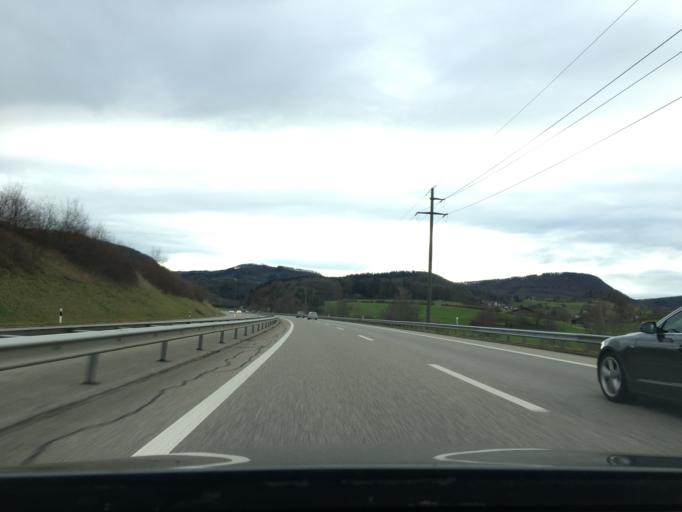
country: CH
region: Aargau
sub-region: Bezirk Laufenburg
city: Sulz
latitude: 47.4903
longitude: 8.0844
